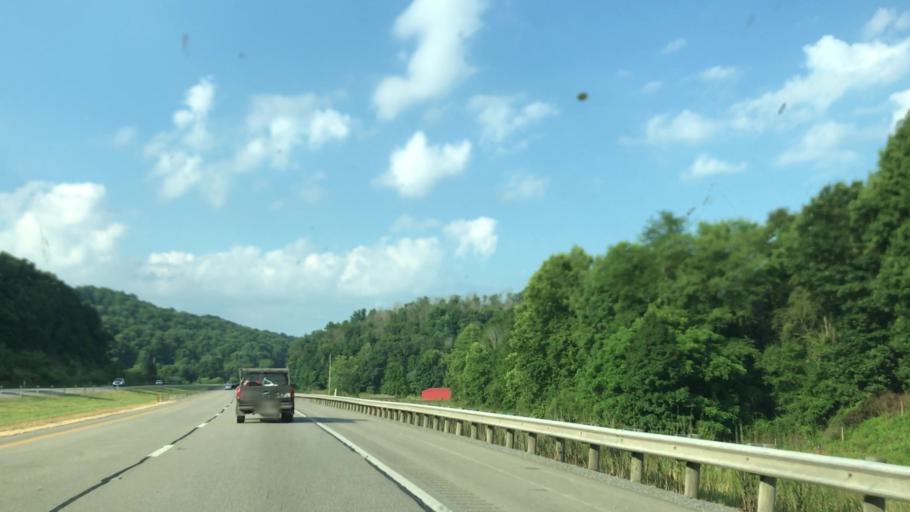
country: US
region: West Virginia
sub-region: Harrison County
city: Stonewood
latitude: 39.2053
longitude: -80.3118
